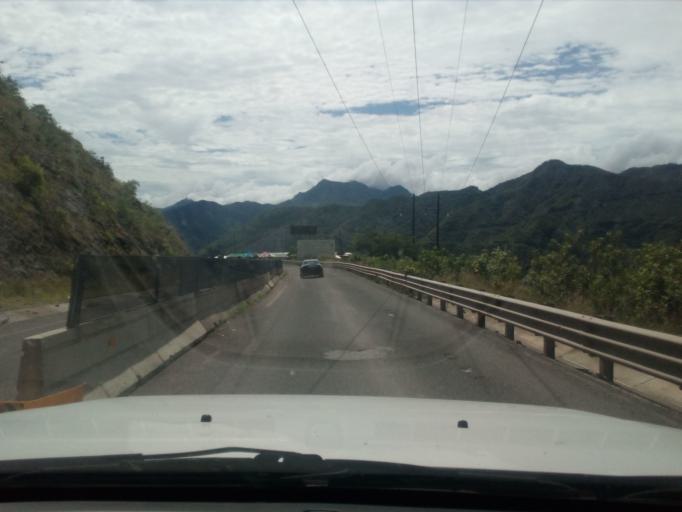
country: MX
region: Durango
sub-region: Pueblo Nuevo
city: La Ciudad
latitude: 23.5445
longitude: -105.7563
